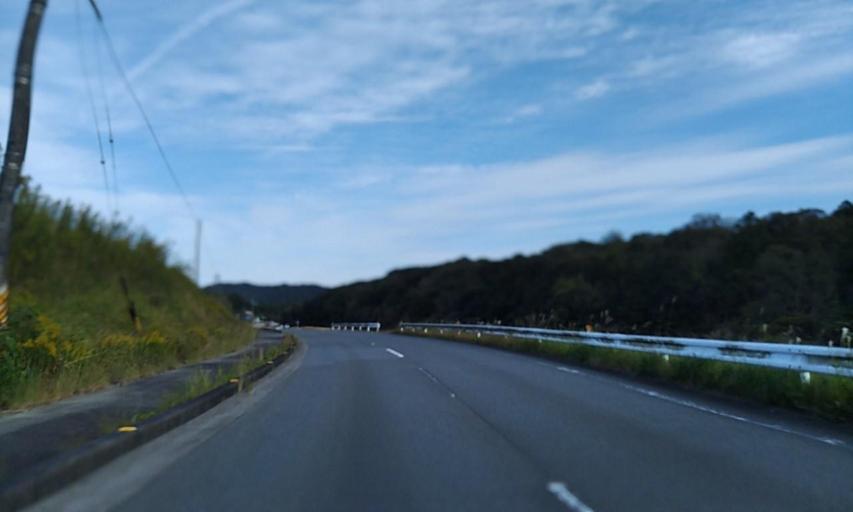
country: JP
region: Mie
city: Ise
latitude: 34.3574
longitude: 136.7590
